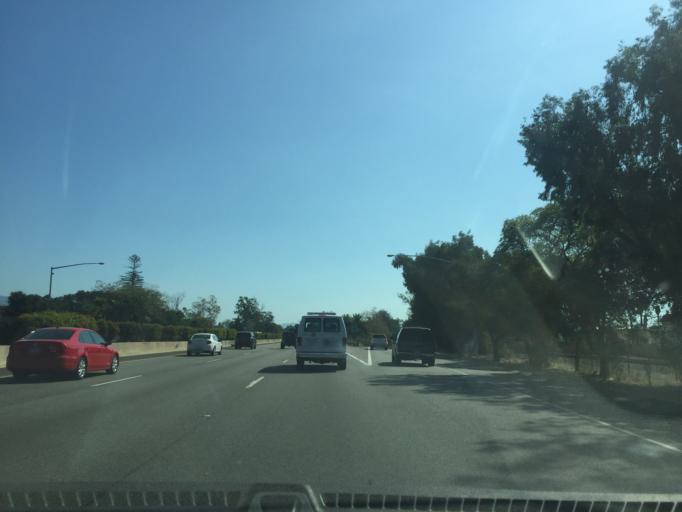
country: US
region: California
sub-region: Santa Barbara County
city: Santa Barbara
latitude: 34.4262
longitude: -119.7241
